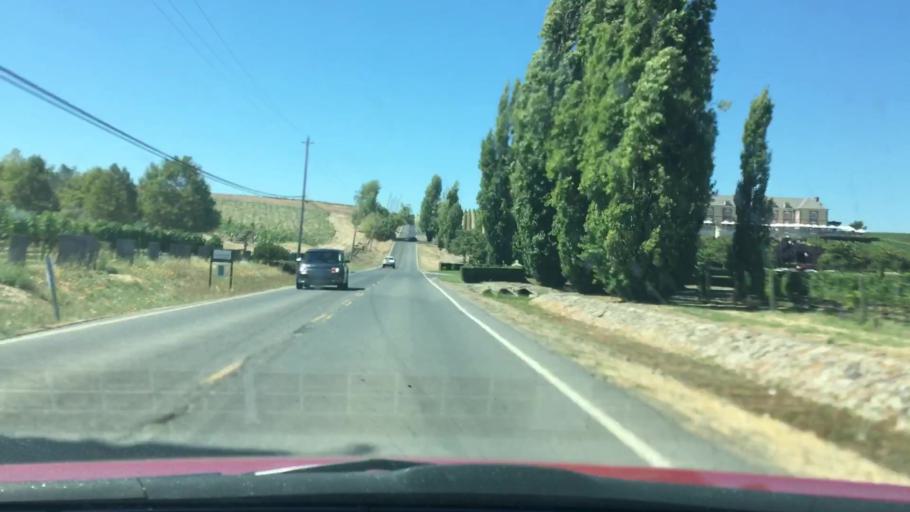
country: US
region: California
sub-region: Napa County
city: Napa
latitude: 38.2554
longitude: -122.3481
